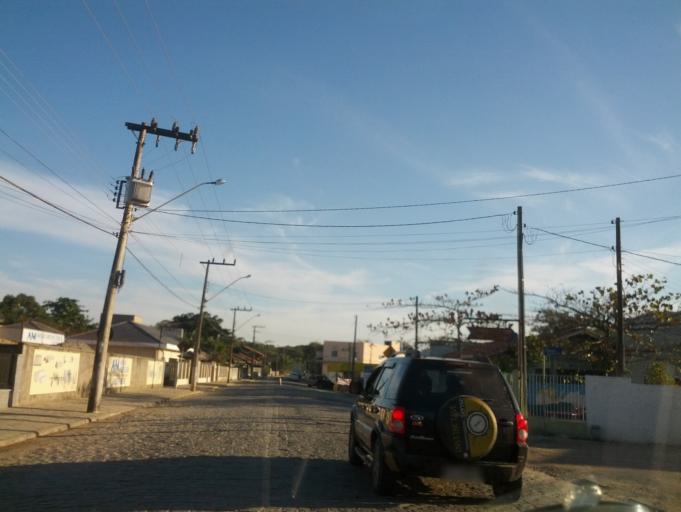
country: BR
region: Santa Catarina
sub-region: Indaial
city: Indaial
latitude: -26.9031
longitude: -49.2588
